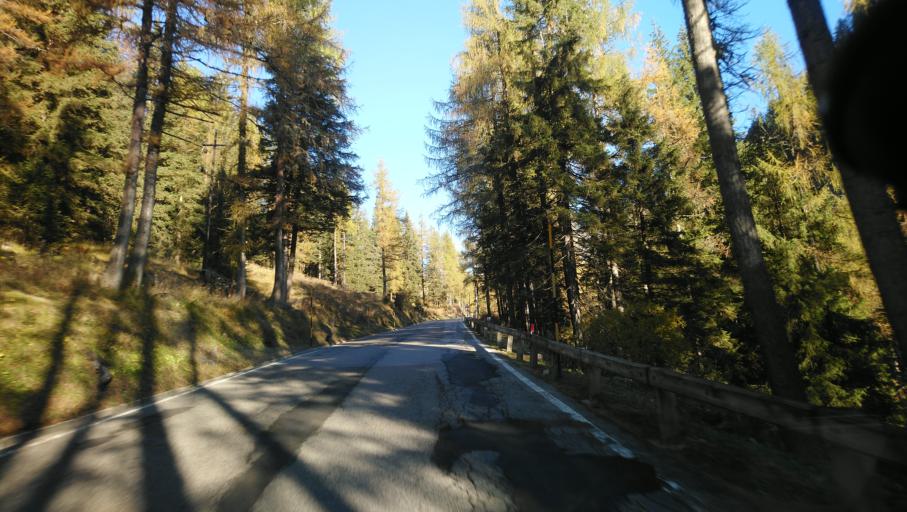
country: IT
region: Veneto
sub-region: Provincia di Belluno
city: Falcade Alto
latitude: 46.3688
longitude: 11.8276
